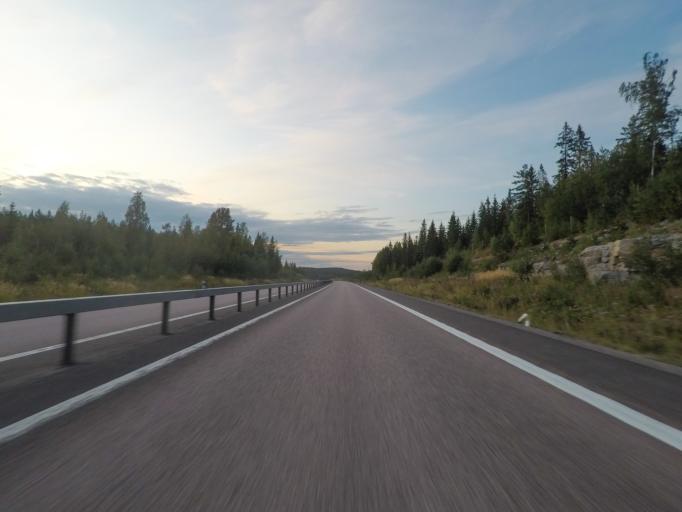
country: FI
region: Central Finland
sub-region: Jyvaeskylae
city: Saeynaetsalo
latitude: 62.1833
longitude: 25.9058
